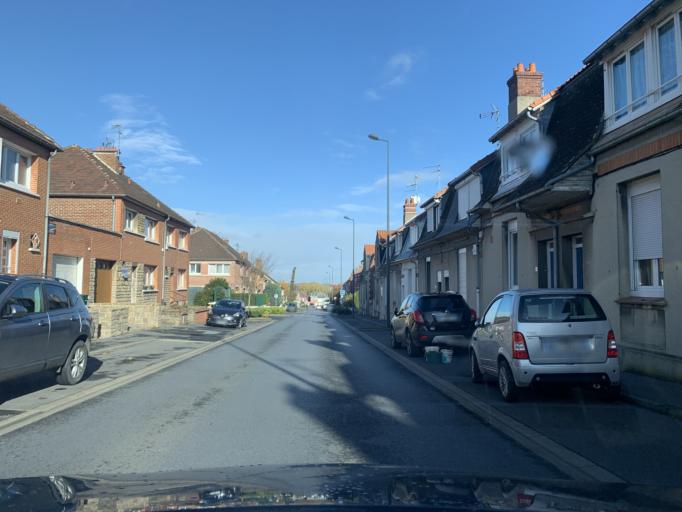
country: FR
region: Nord-Pas-de-Calais
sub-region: Departement du Nord
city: Cambrai
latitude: 50.1795
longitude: 3.2534
